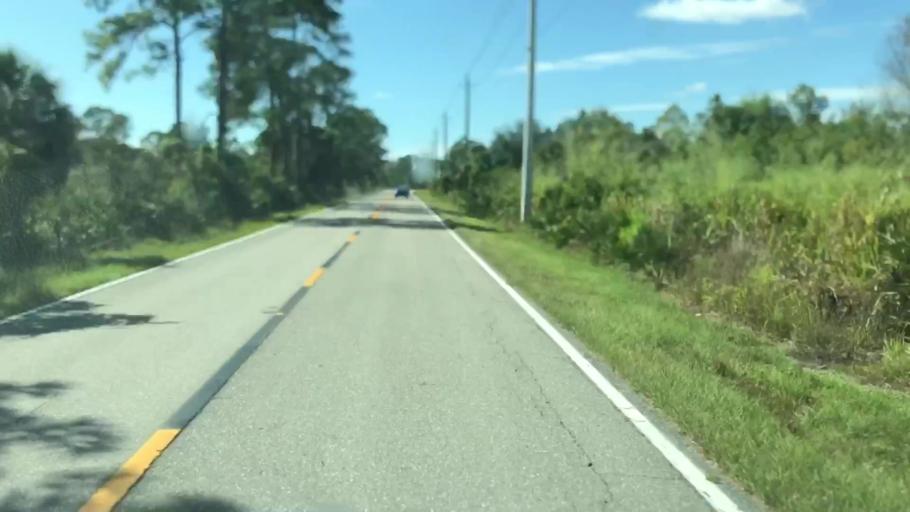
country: US
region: Florida
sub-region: Lee County
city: Olga
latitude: 26.7250
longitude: -81.6615
